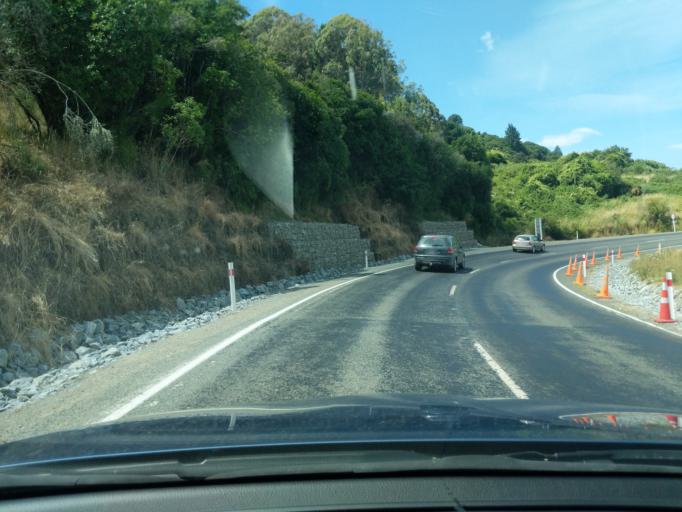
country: NZ
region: Tasman
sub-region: Tasman District
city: Motueka
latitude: -41.0549
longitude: 172.9655
